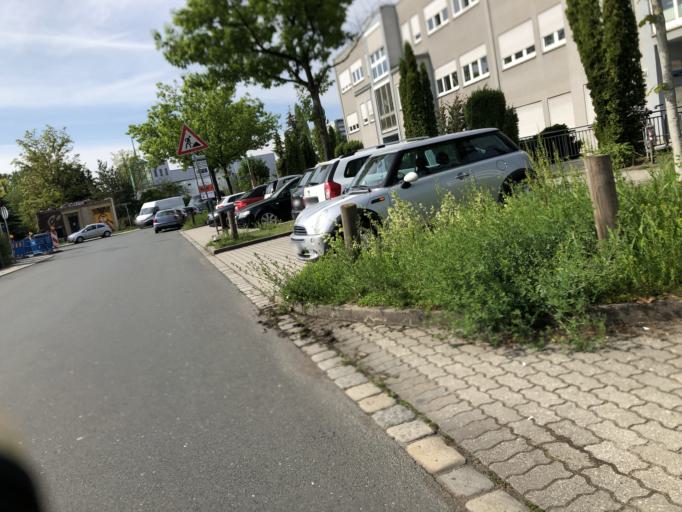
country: DE
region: Bavaria
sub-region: Regierungsbezirk Mittelfranken
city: Erlangen
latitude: 49.5432
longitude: 11.0254
